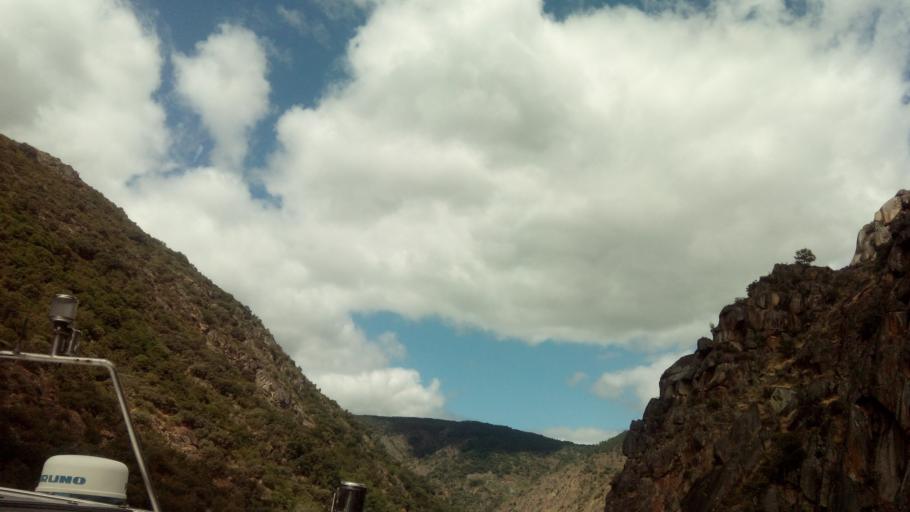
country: ES
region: Galicia
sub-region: Provincia de Lugo
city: Lobios
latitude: 42.3936
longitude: -7.5577
